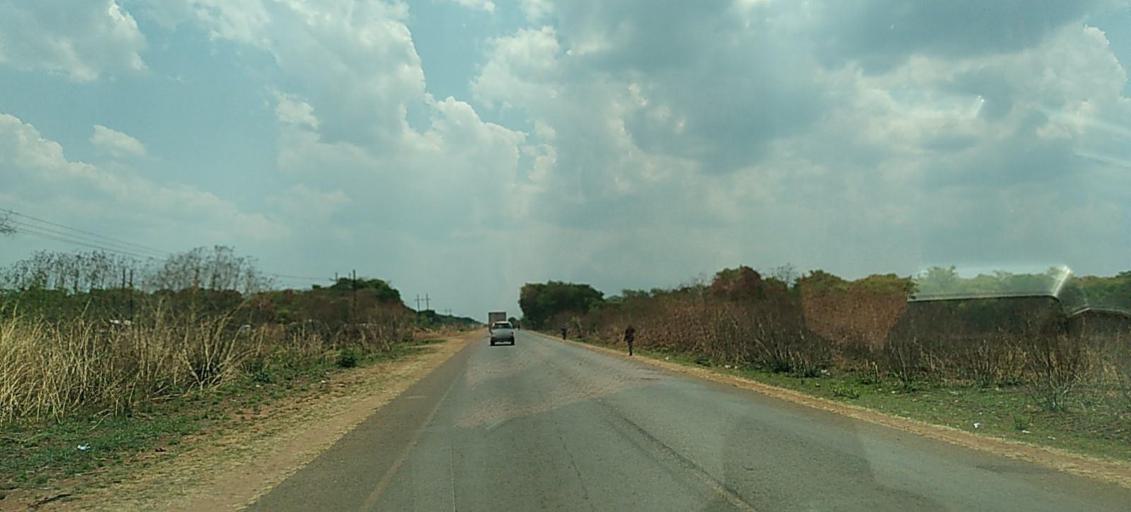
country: ZM
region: Copperbelt
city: Kalulushi
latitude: -12.8351
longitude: 27.9594
